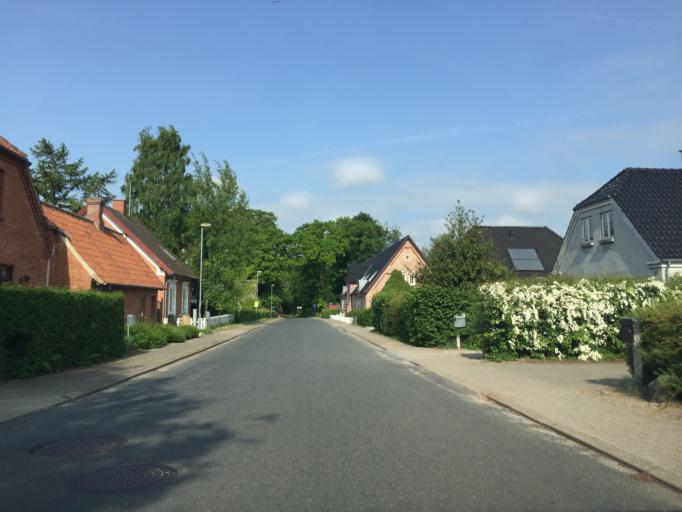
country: DK
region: South Denmark
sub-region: Svendborg Kommune
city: Thuro By
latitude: 55.1397
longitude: 10.7815
